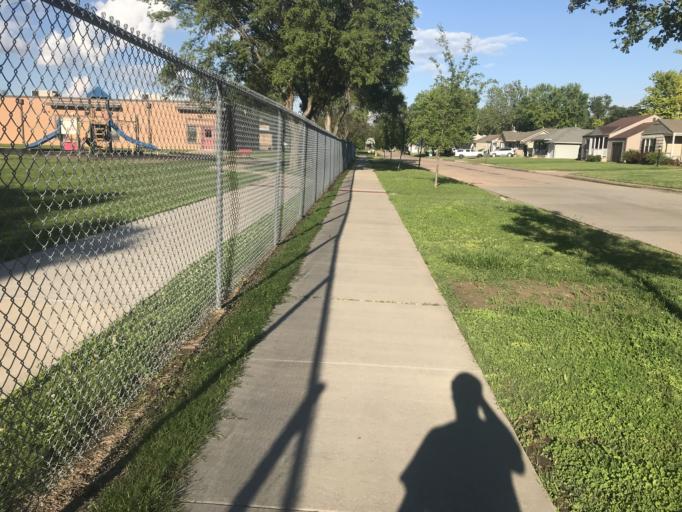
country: US
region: Kansas
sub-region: Saline County
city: Salina
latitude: 38.8163
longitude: -97.6027
